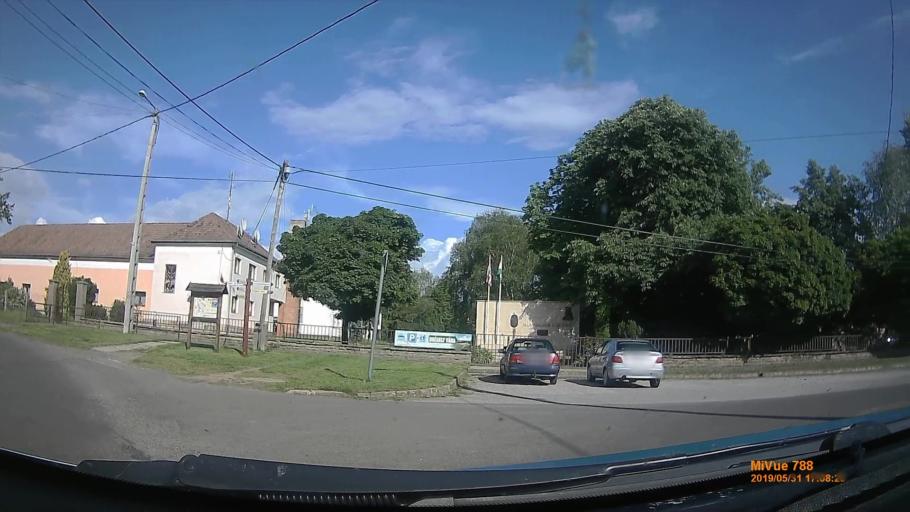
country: HU
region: Nograd
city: Nagyoroszi
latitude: 48.0492
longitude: 19.0536
